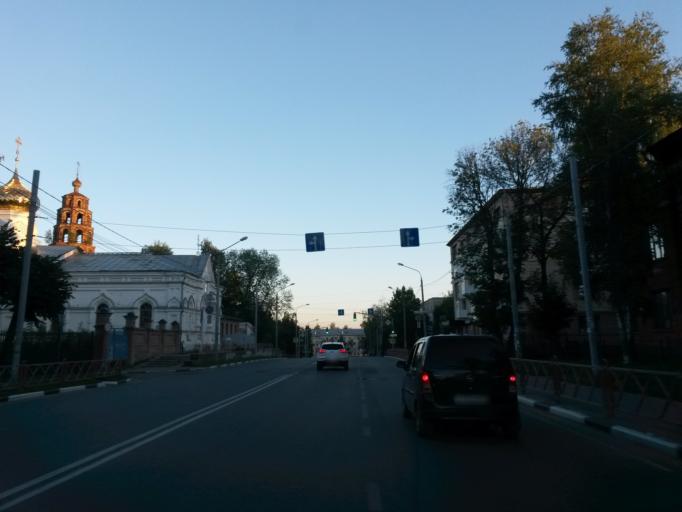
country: RU
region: Jaroslavl
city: Yaroslavl
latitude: 57.6244
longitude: 39.8679
